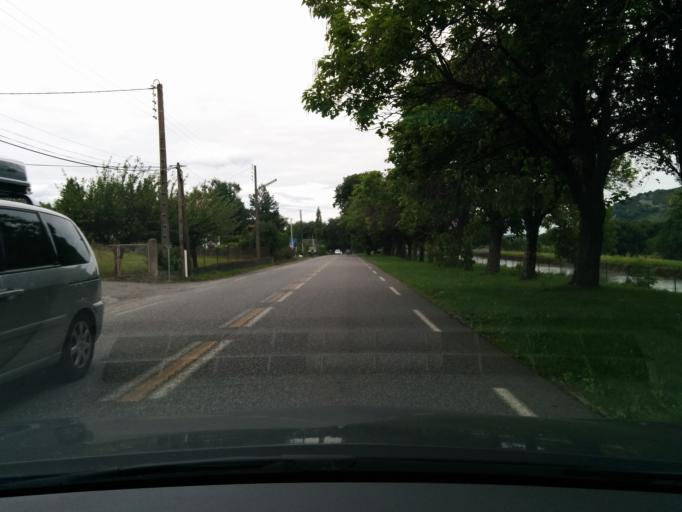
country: FR
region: Midi-Pyrenees
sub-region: Departement des Hautes-Pyrenees
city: La Barthe-de-Neste
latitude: 43.0224
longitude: 0.3719
